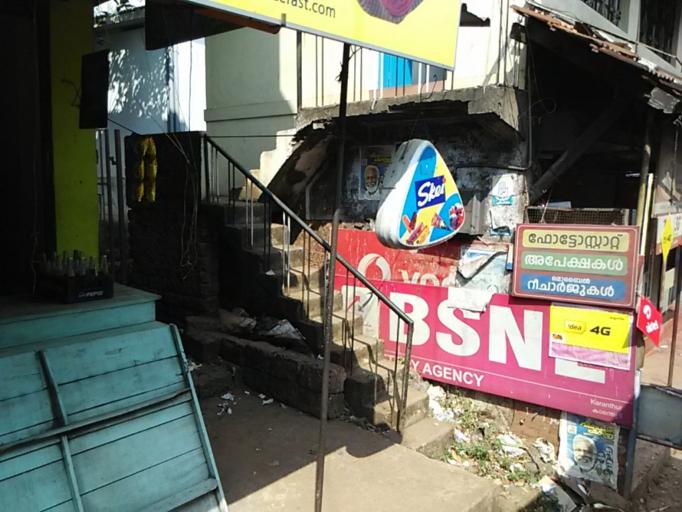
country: IN
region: Kerala
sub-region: Kozhikode
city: Kunnamangalam
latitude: 11.3012
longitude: 75.8615
